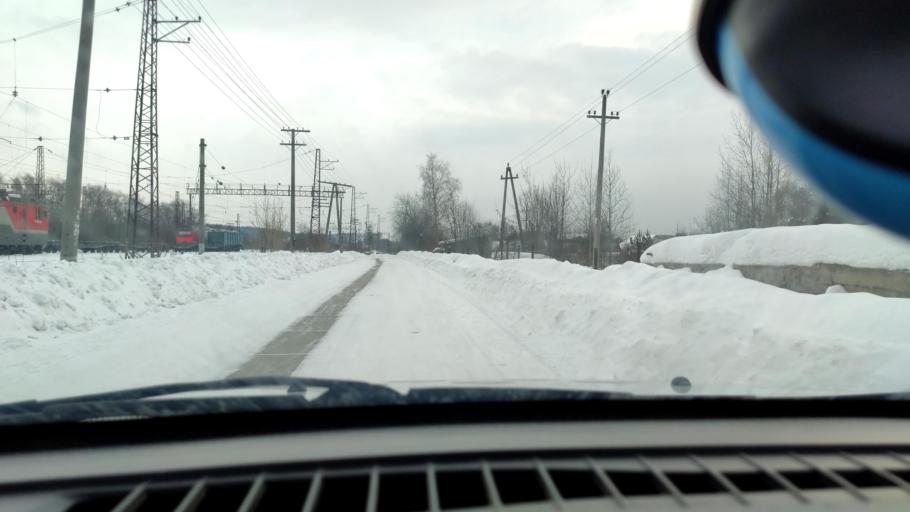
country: RU
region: Perm
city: Overyata
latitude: 58.0847
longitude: 55.8686
